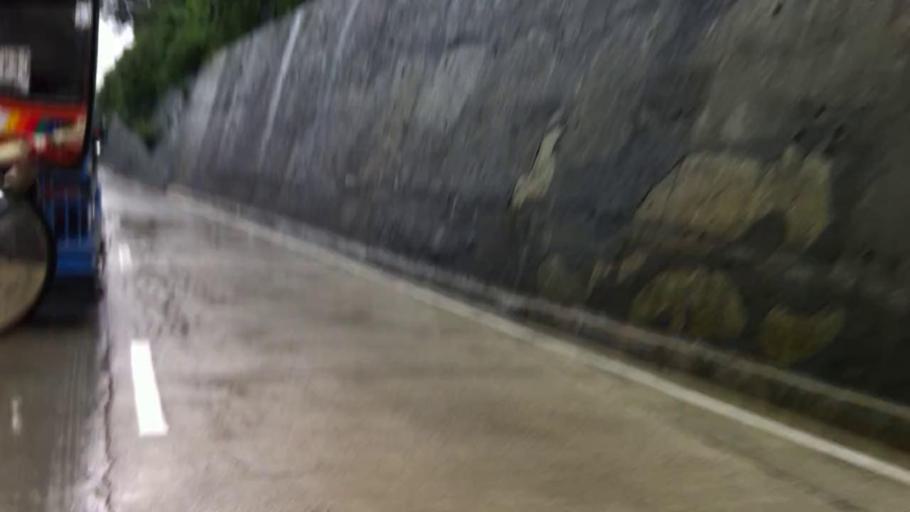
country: PH
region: Cordillera
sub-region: Baguio City
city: Baguio
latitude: 16.4313
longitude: 120.5973
